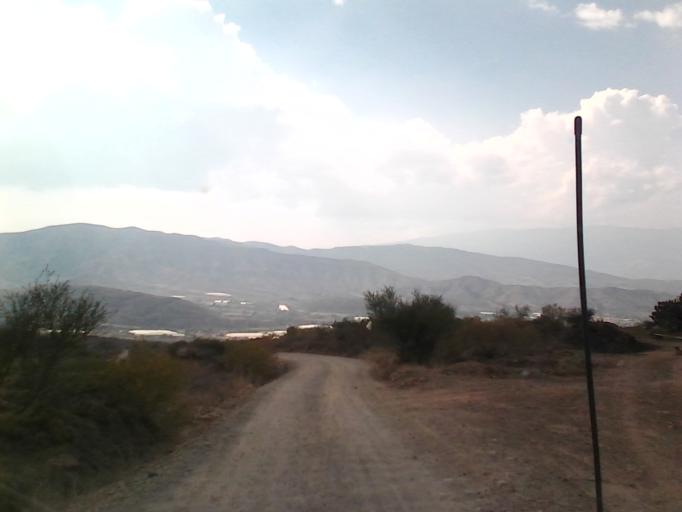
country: CO
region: Boyaca
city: Sachica
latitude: 5.5747
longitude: -73.5212
